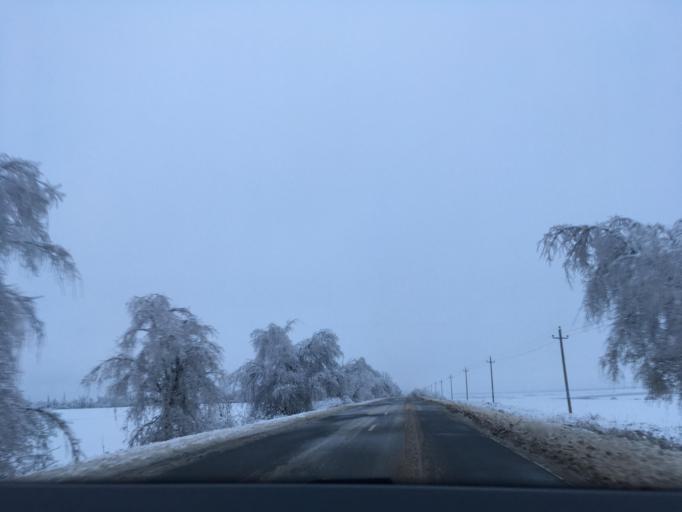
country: RU
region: Voronezj
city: Verkhniy Mamon
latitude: 50.0234
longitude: 40.0800
